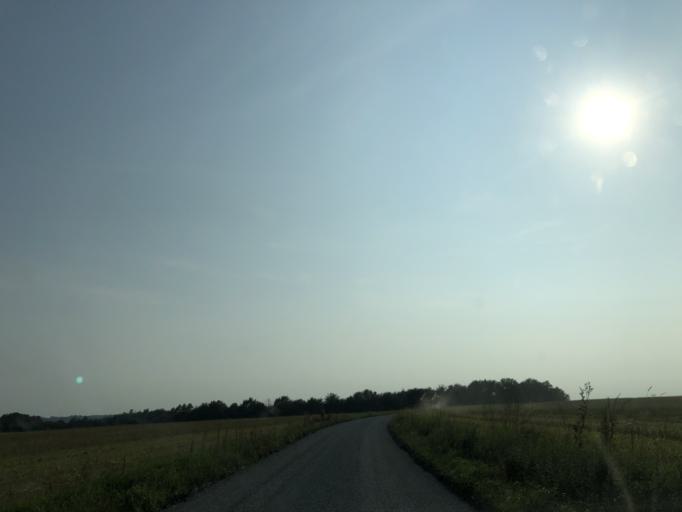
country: DK
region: Central Jutland
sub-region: Favrskov Kommune
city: Hammel
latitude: 56.2382
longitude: 9.7580
